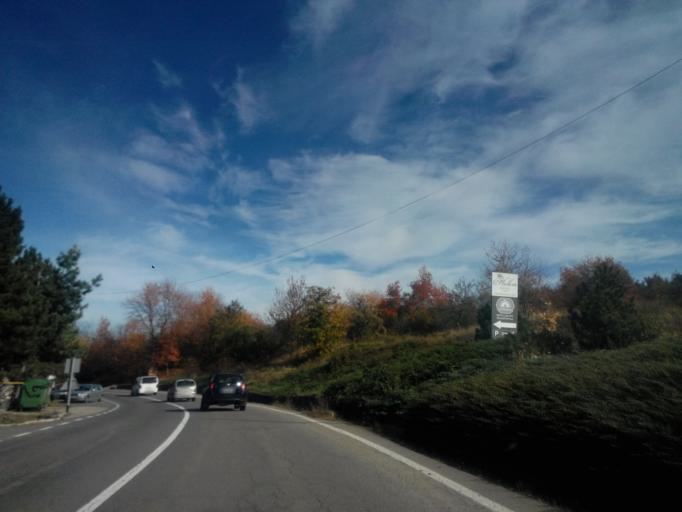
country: RO
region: Bacau
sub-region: Comuna Luizi-Calugara
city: Osebiti
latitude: 46.5512
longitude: 26.8251
